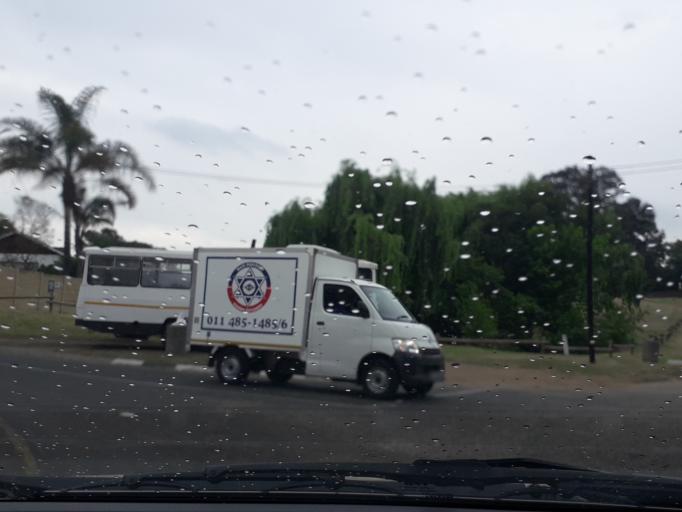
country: ZA
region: Gauteng
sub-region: City of Johannesburg Metropolitan Municipality
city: Modderfontein
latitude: -26.1332
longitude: 28.1033
